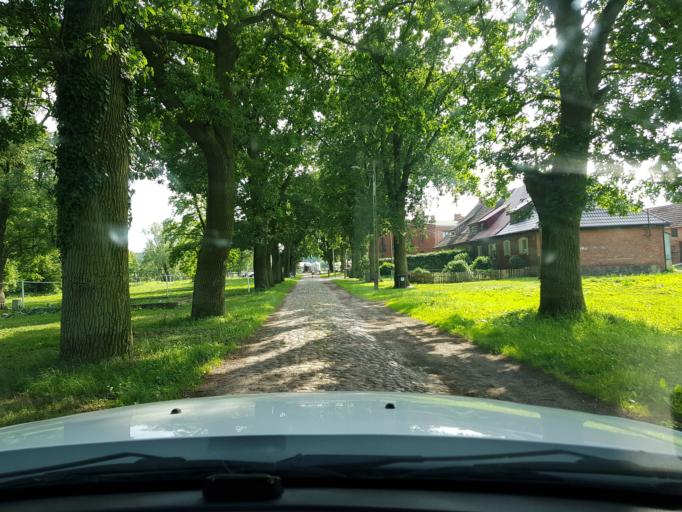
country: PL
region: West Pomeranian Voivodeship
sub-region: Powiat gryfinski
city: Chojna
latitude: 52.9981
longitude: 14.4839
